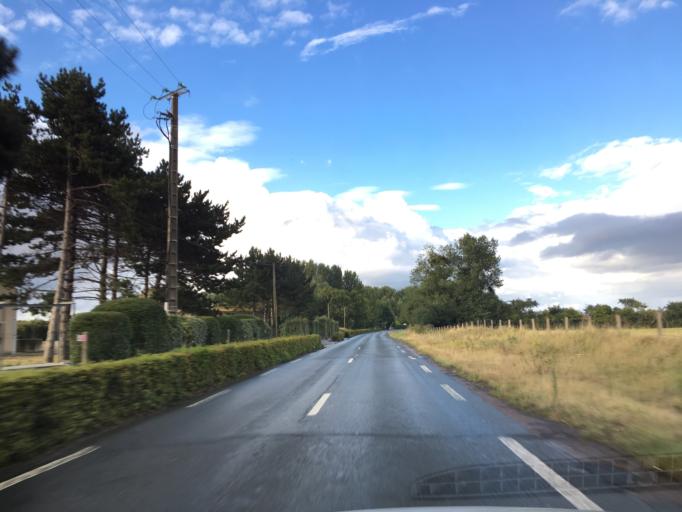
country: FR
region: Lower Normandy
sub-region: Departement du Calvados
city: Merville-Franceville-Plage
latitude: 49.2721
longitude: -0.2173
